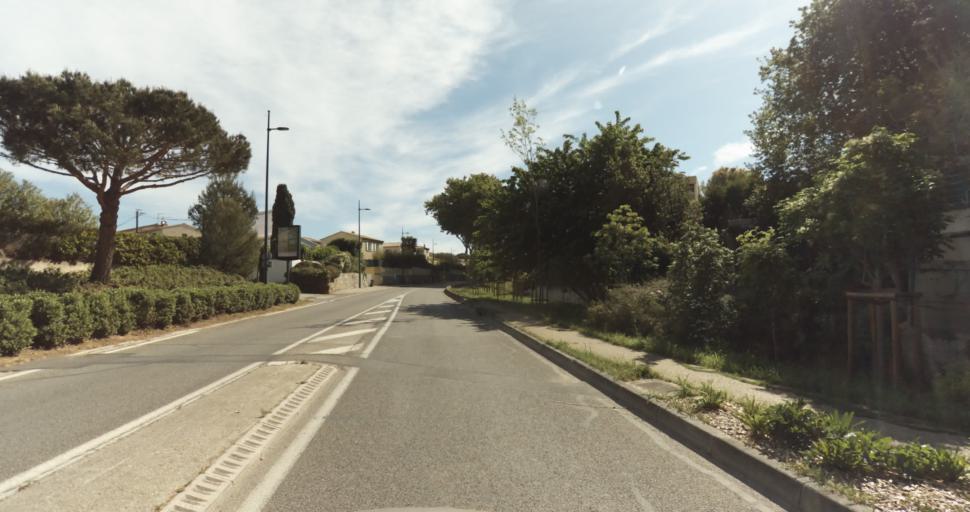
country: FR
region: Provence-Alpes-Cote d'Azur
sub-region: Departement du Var
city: Sanary-sur-Mer
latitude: 43.1074
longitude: 5.8227
